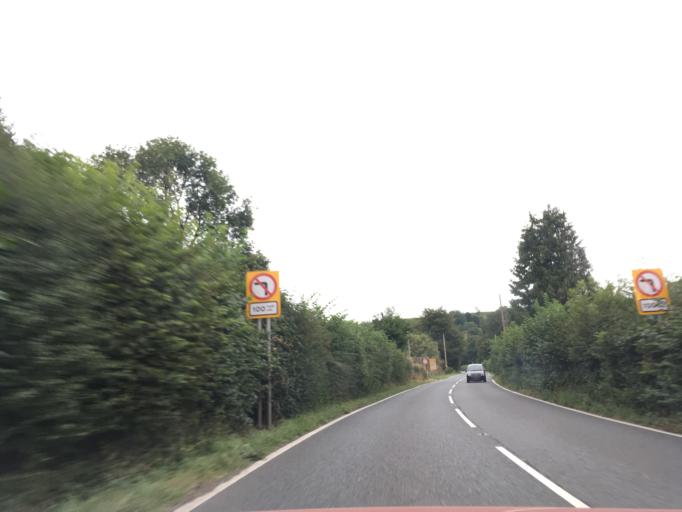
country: GB
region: Wales
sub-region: Blaenau Gwent
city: Brynmawr
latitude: 51.8857
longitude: -3.2362
